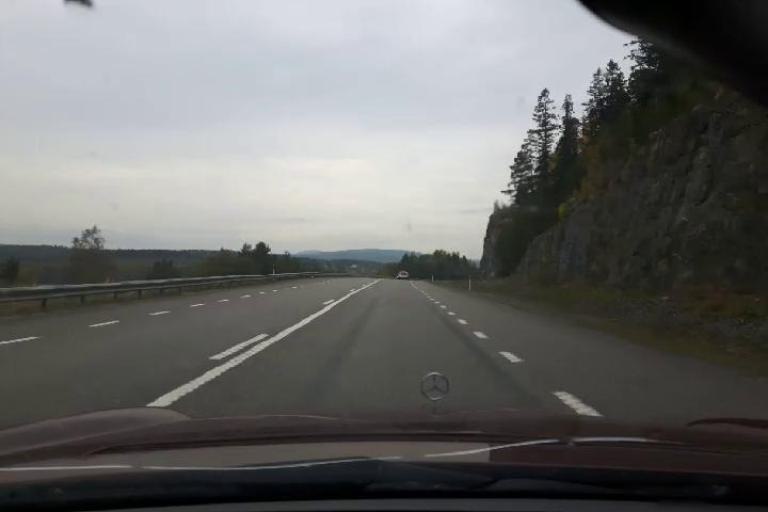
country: SE
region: Vaesternorrland
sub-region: Kramfors Kommun
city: Nordingra
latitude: 63.0075
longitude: 18.2273
